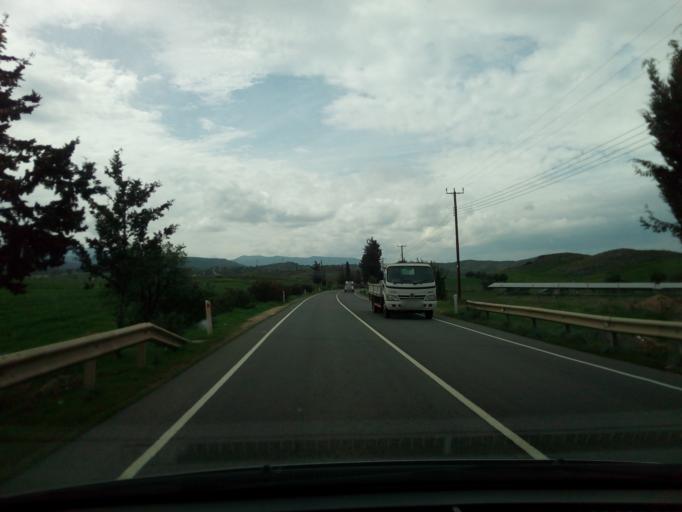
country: CY
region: Lefkosia
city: Astromeritis
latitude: 35.0860
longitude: 32.9576
